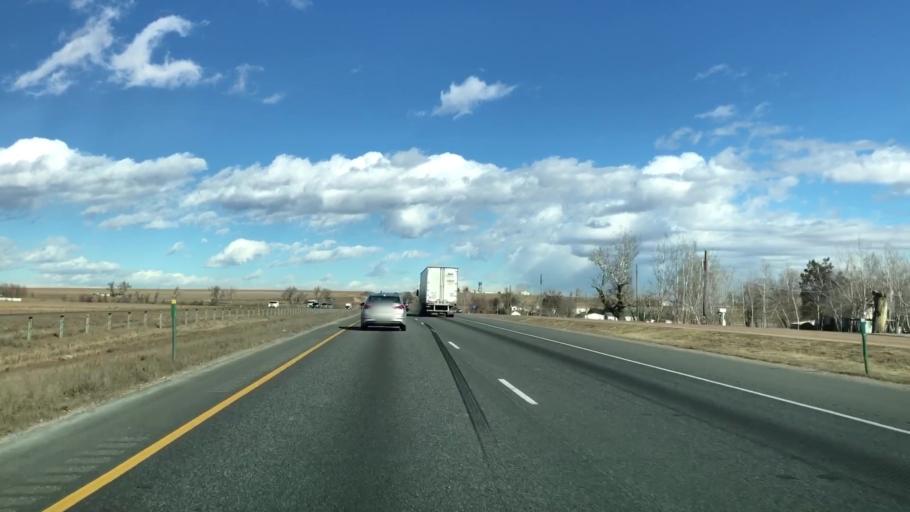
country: US
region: Colorado
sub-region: Weld County
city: Mead
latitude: 40.2526
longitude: -104.9788
